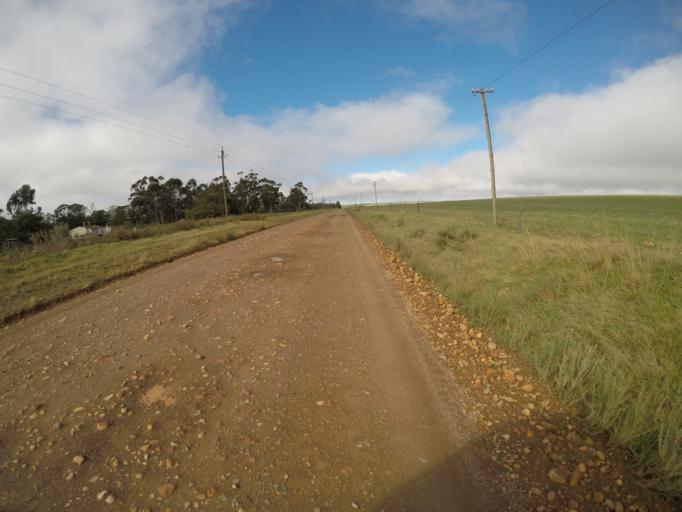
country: ZA
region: Western Cape
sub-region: Cape Winelands District Municipality
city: Ashton
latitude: -34.1375
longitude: 19.8598
